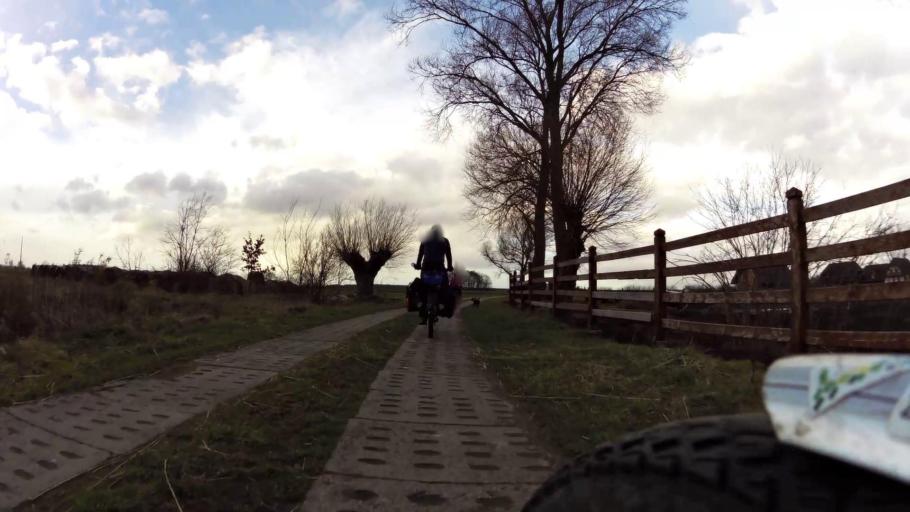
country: PL
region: West Pomeranian Voivodeship
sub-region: Powiat kamienski
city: Kamien Pomorski
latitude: 53.8931
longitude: 14.7209
